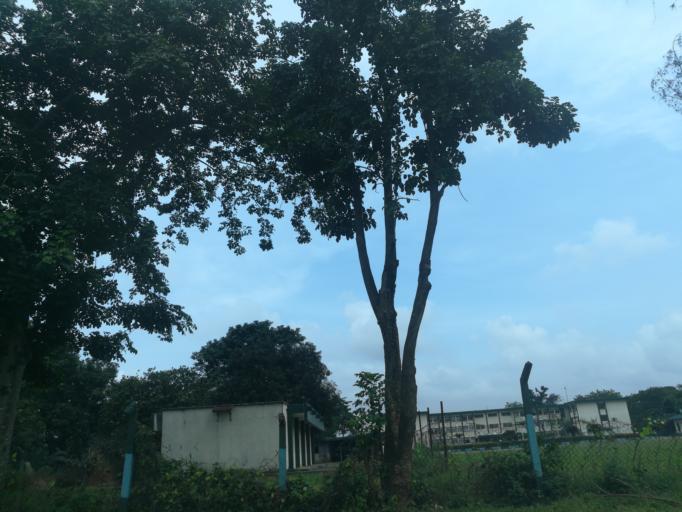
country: NG
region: Lagos
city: Oshodi
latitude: 6.5636
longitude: 3.3603
